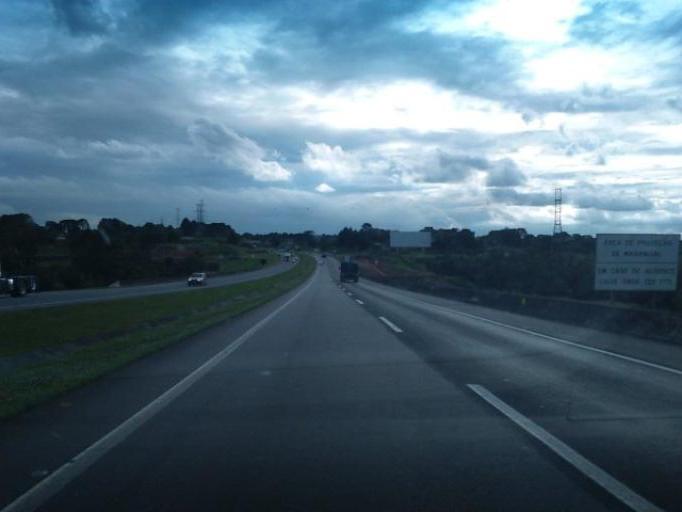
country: BR
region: Parana
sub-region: Piraquara
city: Piraquara
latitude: -25.4801
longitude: -49.1025
